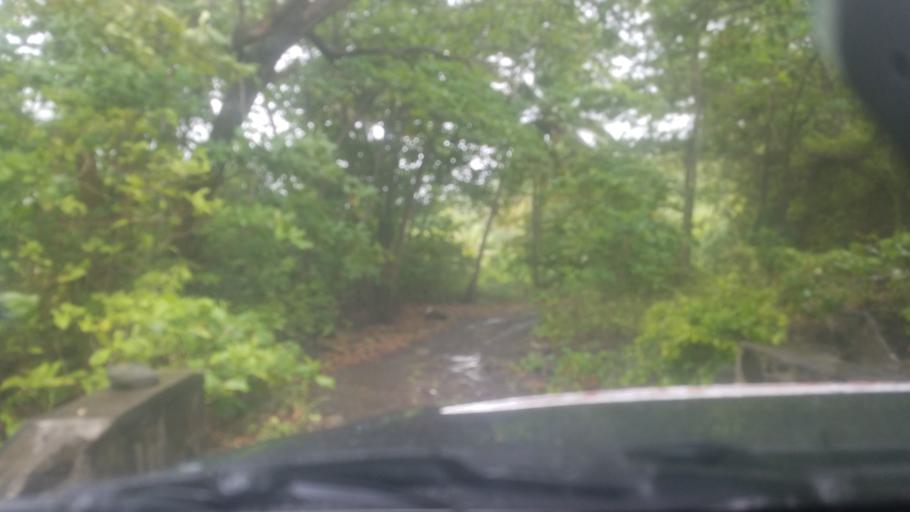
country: LC
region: Gros-Islet
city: Gros Islet
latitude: 14.0397
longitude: -60.8982
